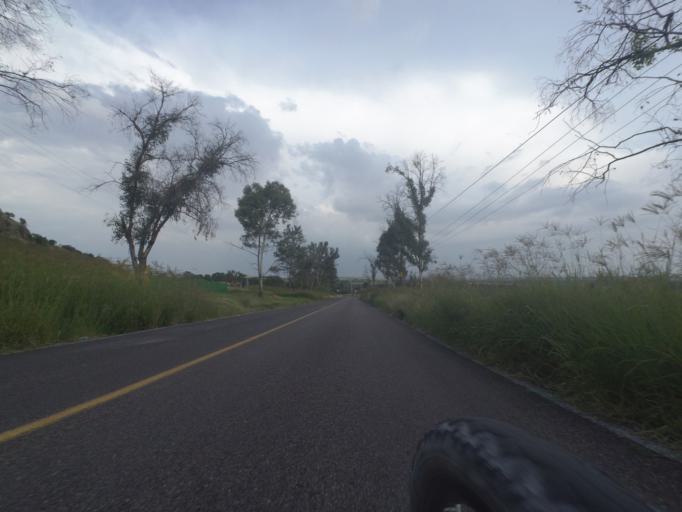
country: MX
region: Aguascalientes
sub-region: Aguascalientes
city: La Loma de los Negritos
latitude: 21.8370
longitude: -102.3738
